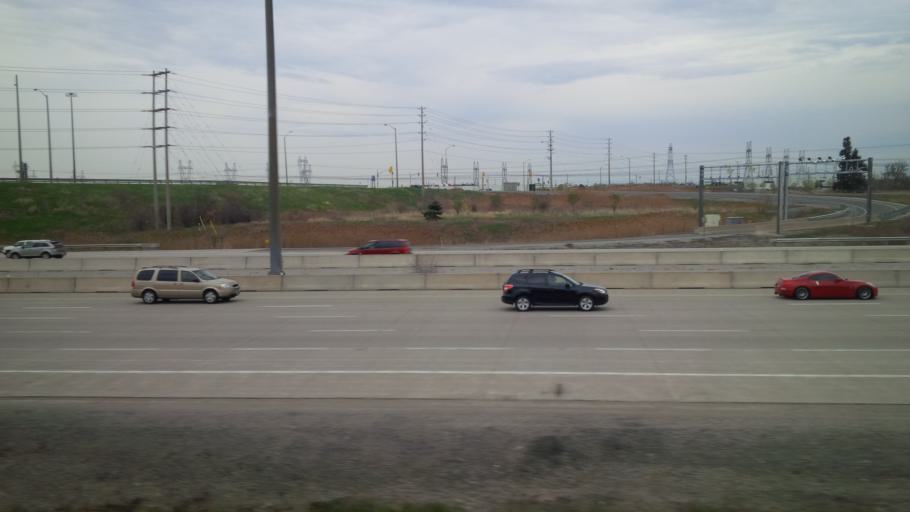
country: CA
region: Ontario
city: Brampton
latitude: 43.6866
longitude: -79.6922
